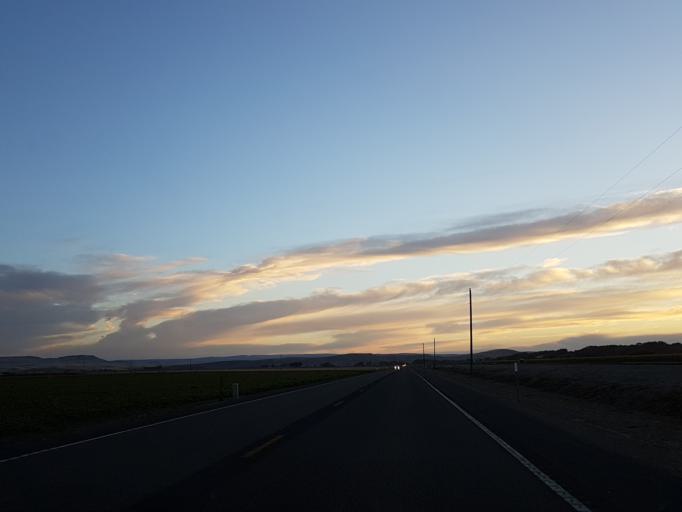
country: US
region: Oregon
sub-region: Malheur County
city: Vale
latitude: 43.9590
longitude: -117.2829
